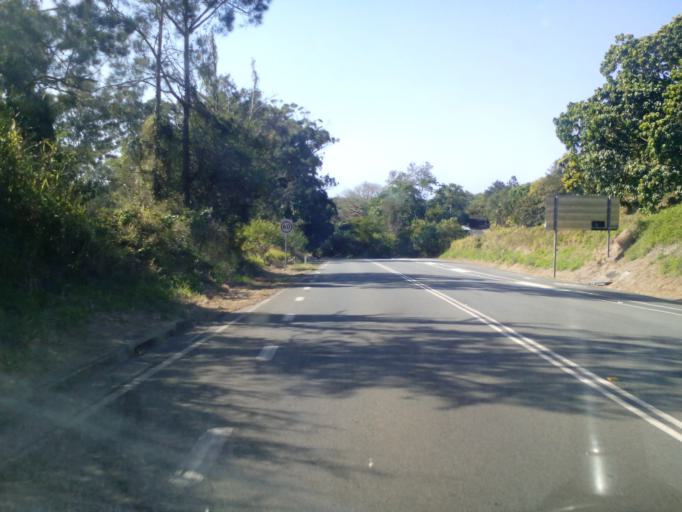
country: AU
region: New South Wales
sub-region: Tweed
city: Kingscliff
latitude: -28.2626
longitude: 153.5705
